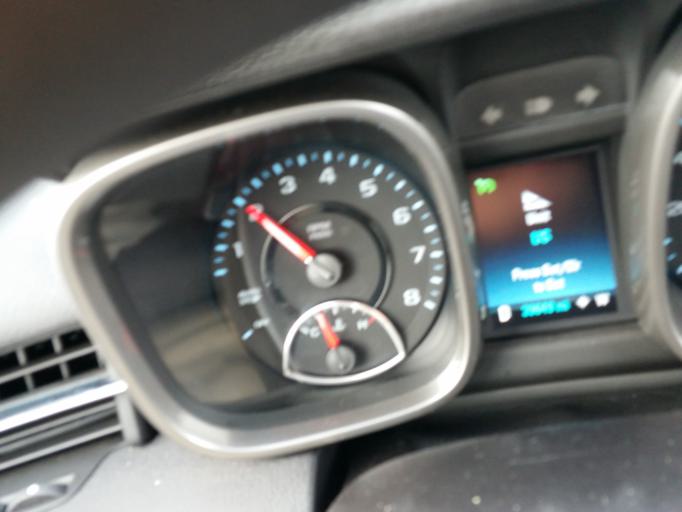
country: US
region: Iowa
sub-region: Delaware County
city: Manchester
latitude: 42.4640
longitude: -91.5435
